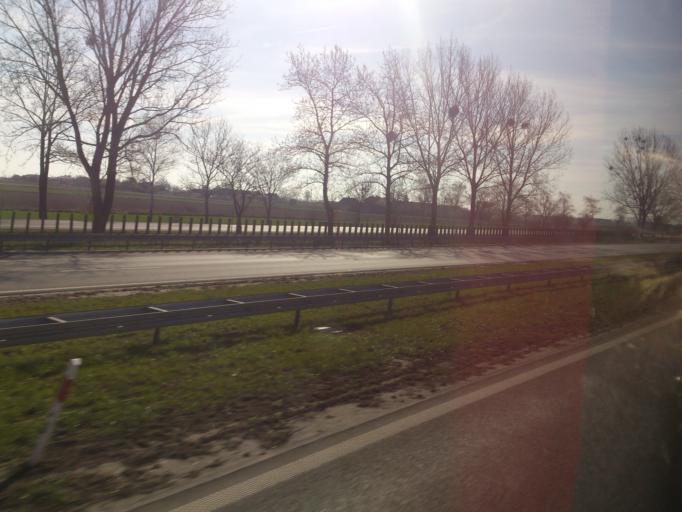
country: PL
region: Kujawsko-Pomorskie
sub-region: Powiat aleksandrowski
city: Raciazek
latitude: 52.8355
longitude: 18.7979
